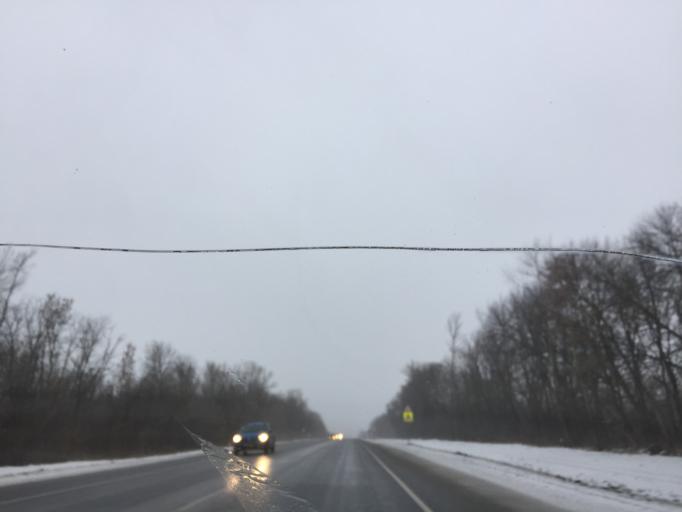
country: RU
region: Tula
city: Plavsk
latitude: 53.7351
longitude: 37.3115
